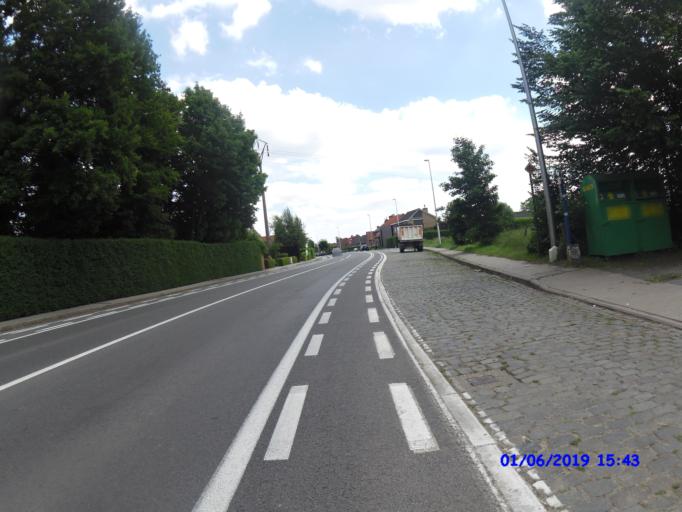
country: BE
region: Flanders
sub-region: Provincie West-Vlaanderen
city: Diksmuide
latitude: 51.0299
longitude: 2.8847
